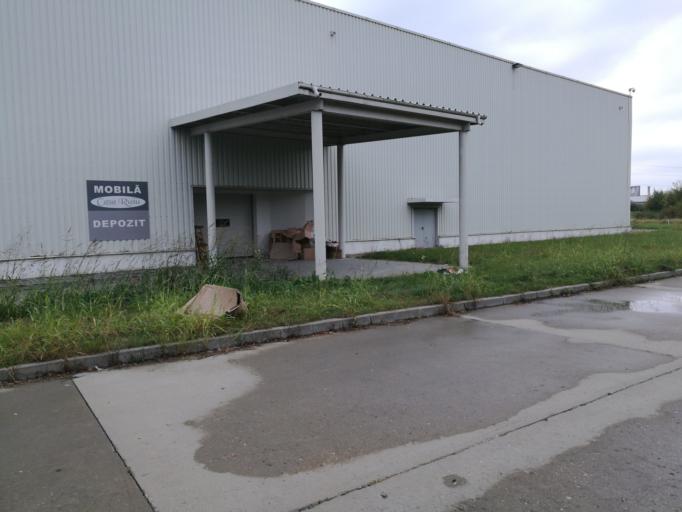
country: RO
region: Arges
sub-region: Oras Stefanesti
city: Golesti
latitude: 44.8200
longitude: 24.9402
